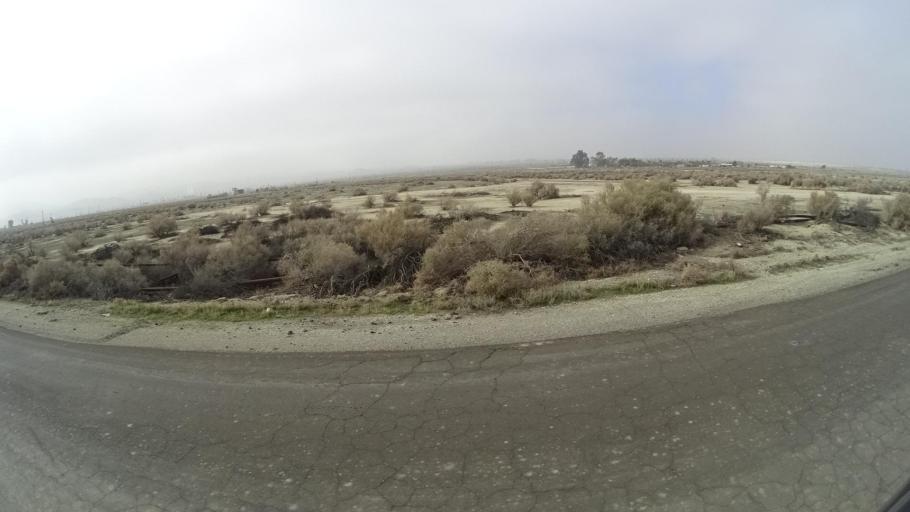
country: US
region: California
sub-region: Kern County
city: Maricopa
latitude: 35.0530
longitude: -119.3671
